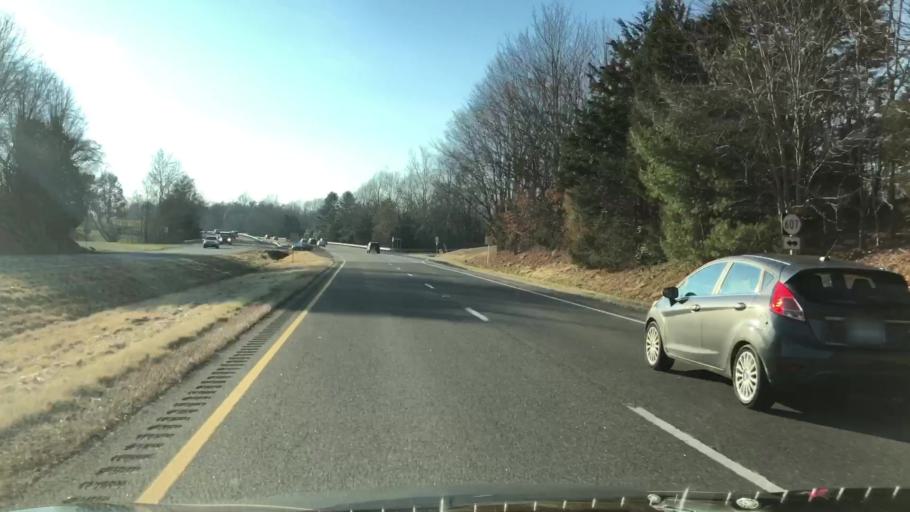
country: US
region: Virginia
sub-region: Madison County
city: Brightwood
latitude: 38.4201
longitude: -78.1961
